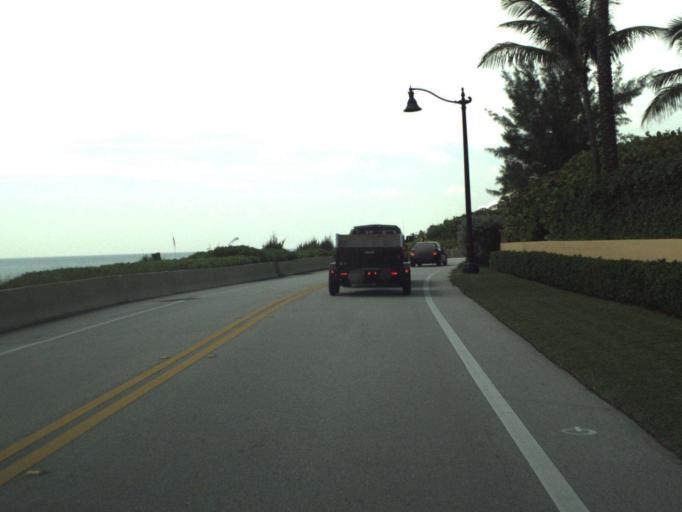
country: US
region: Florida
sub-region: Palm Beach County
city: Lake Worth
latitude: 26.6478
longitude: -80.0373
